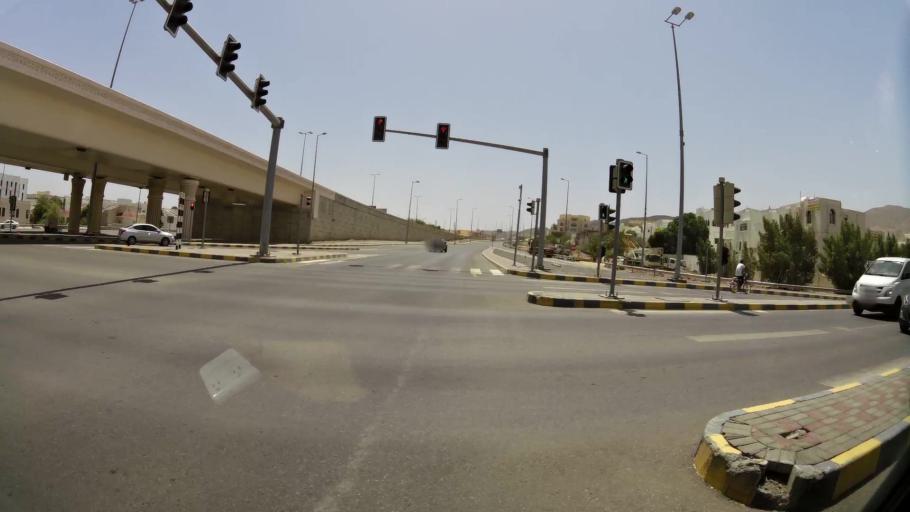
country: OM
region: Muhafazat Masqat
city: Bawshar
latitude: 23.5905
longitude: 58.4473
